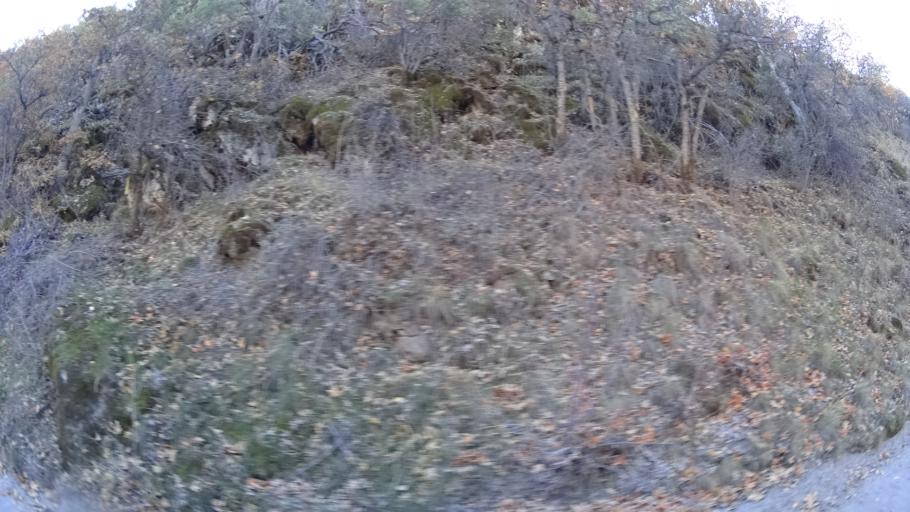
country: US
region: California
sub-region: Siskiyou County
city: Yreka
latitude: 41.8309
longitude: -122.6295
